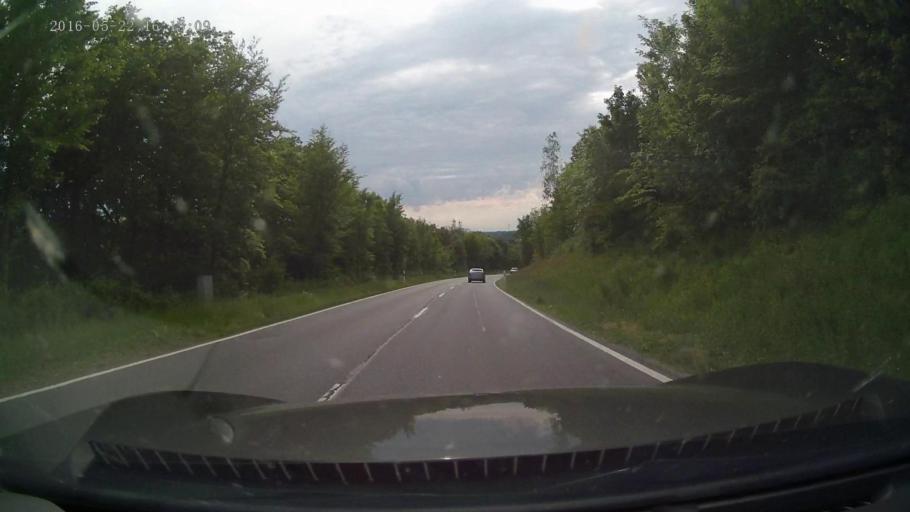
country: DE
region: Baden-Wuerttemberg
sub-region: Karlsruhe Region
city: Osterburken
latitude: 49.4258
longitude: 9.4327
